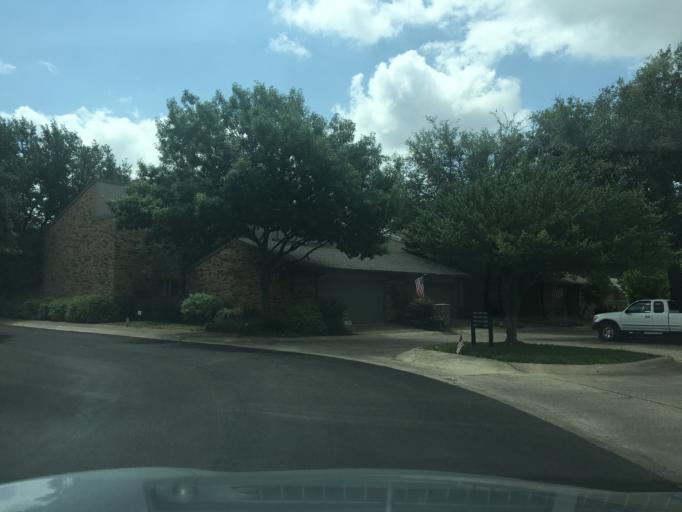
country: US
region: Texas
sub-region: Dallas County
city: Addison
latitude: 32.9189
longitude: -96.8150
